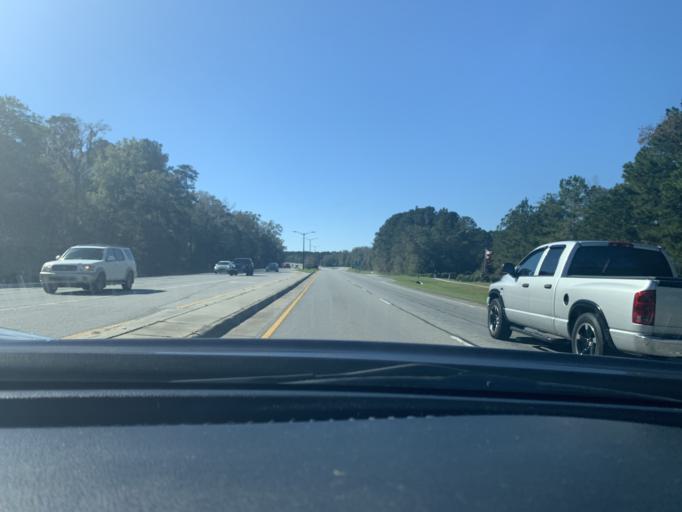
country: US
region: Georgia
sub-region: Chatham County
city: Pooler
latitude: 32.1275
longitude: -81.2611
